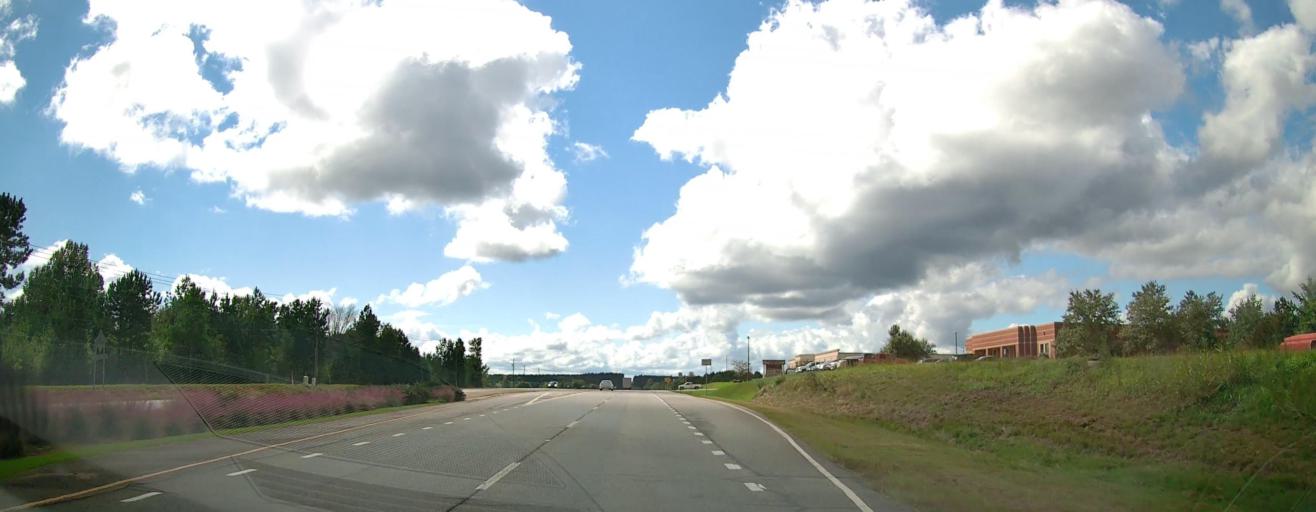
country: US
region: Georgia
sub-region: Baldwin County
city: Milledgeville
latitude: 33.0906
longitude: -83.2821
